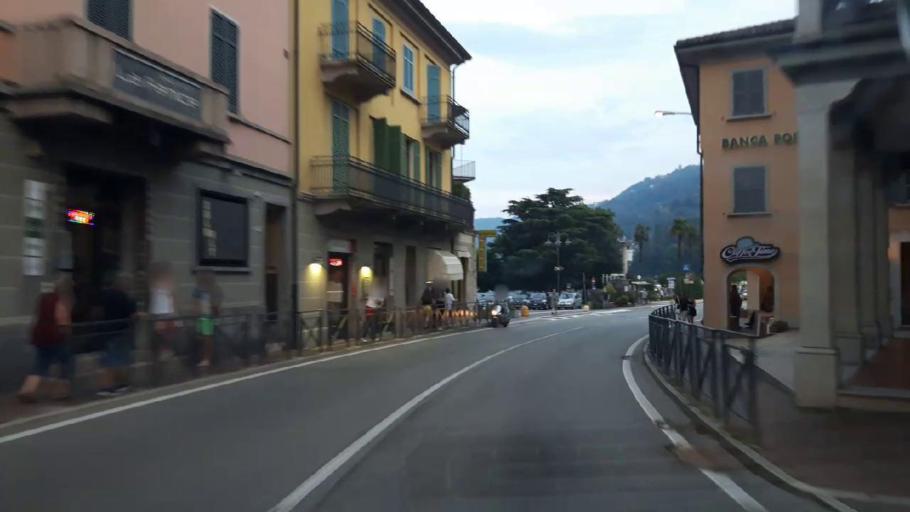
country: IT
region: Piedmont
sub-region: Provincia Verbano-Cusio-Ossola
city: Baveno
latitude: 45.9097
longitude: 8.5055
